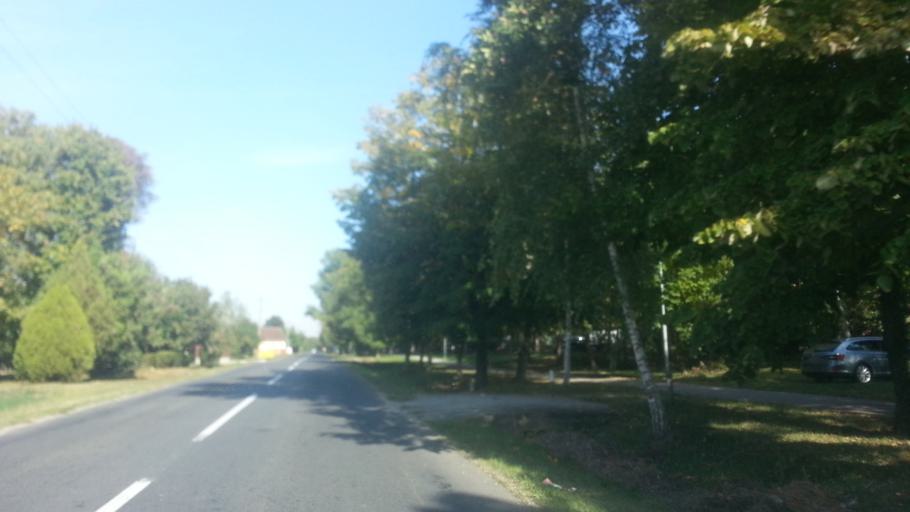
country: RS
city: Belegis
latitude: 45.0037
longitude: 20.3072
